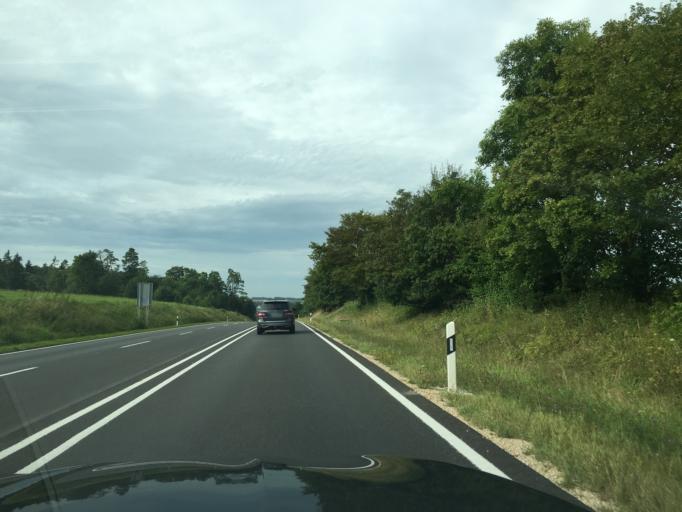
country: DE
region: Baden-Wuerttemberg
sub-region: Tuebingen Region
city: Rechtenstein
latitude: 48.2267
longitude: 9.5511
